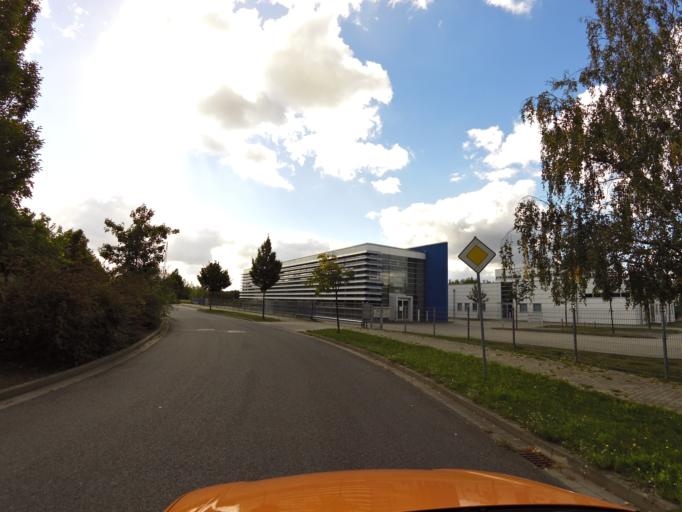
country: DE
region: Brandenburg
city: Luckenwalde
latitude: 52.0955
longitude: 13.1319
